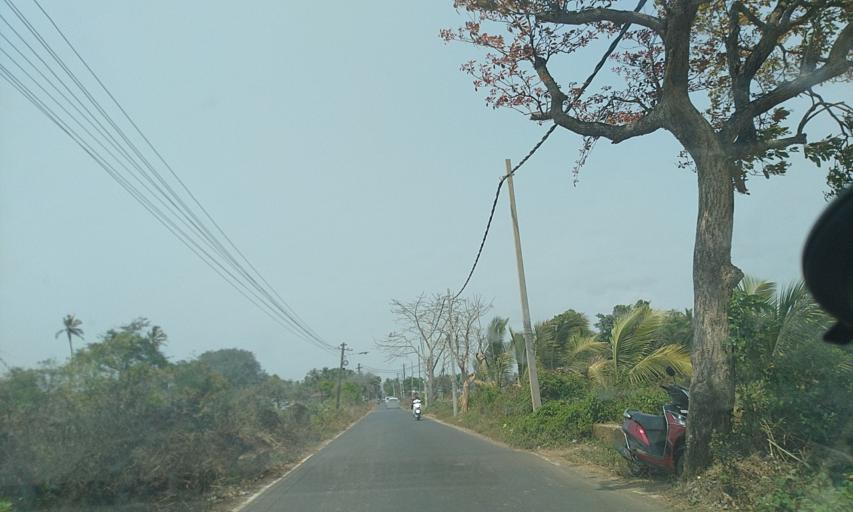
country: IN
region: Goa
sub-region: North Goa
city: Saligao
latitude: 15.5485
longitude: 73.8062
